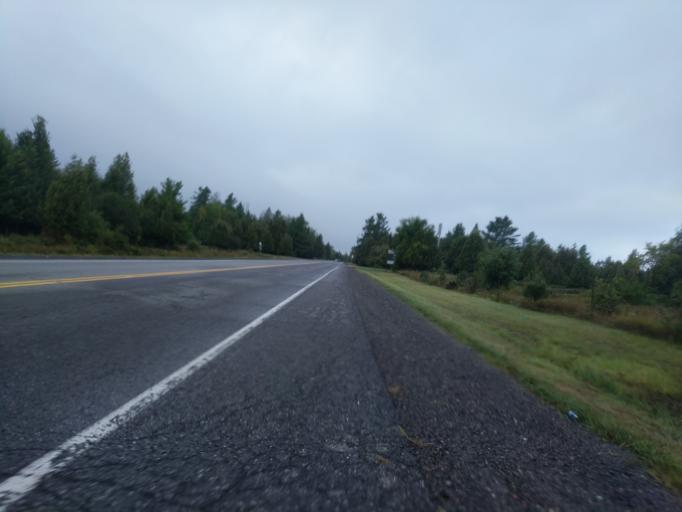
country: CA
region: Ontario
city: Bells Corners
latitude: 45.3173
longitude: -75.8610
